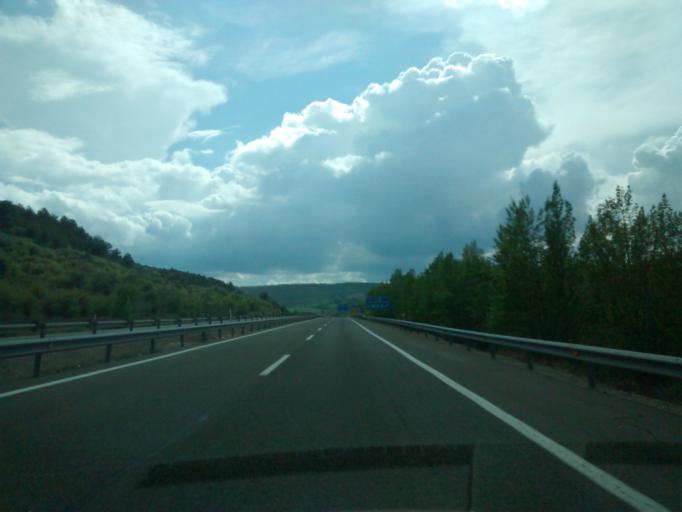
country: ES
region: Castille and Leon
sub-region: Provincia de Soria
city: Medinaceli
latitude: 41.1751
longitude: -2.4049
